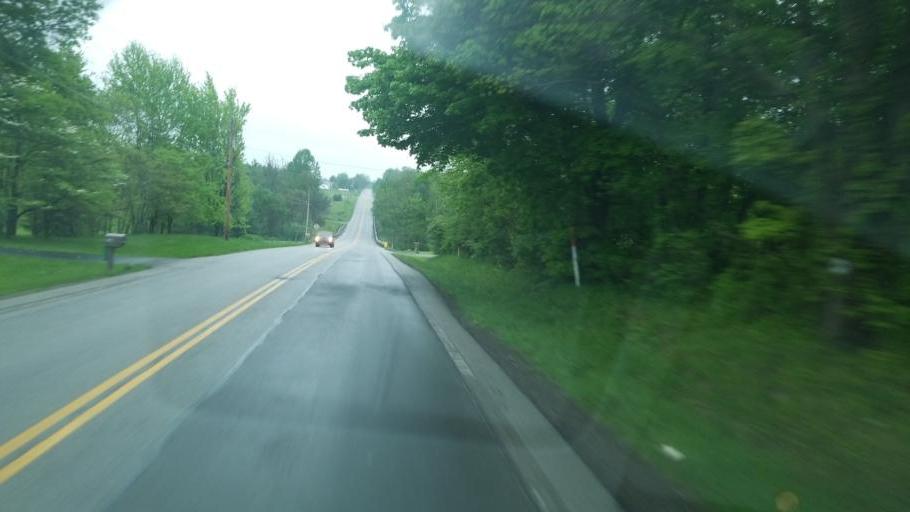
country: US
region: Ohio
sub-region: Highland County
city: Hillsboro
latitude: 39.2624
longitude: -83.5993
